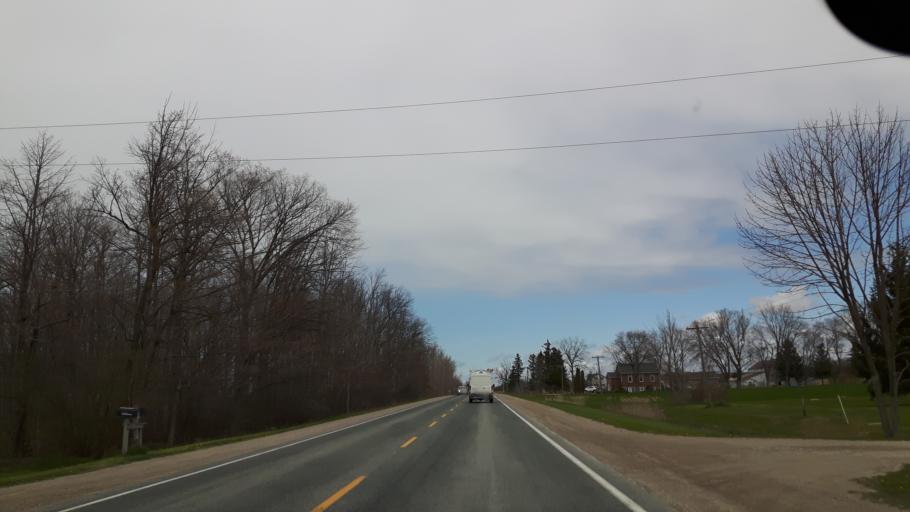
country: CA
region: Ontario
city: Bluewater
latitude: 43.5008
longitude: -81.6955
